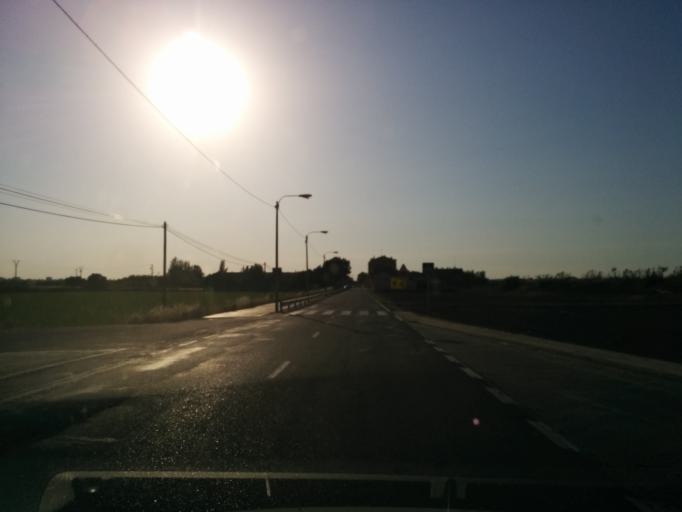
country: ES
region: Aragon
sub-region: Provincia de Zaragoza
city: Zaragoza
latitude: 41.6461
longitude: -0.8158
